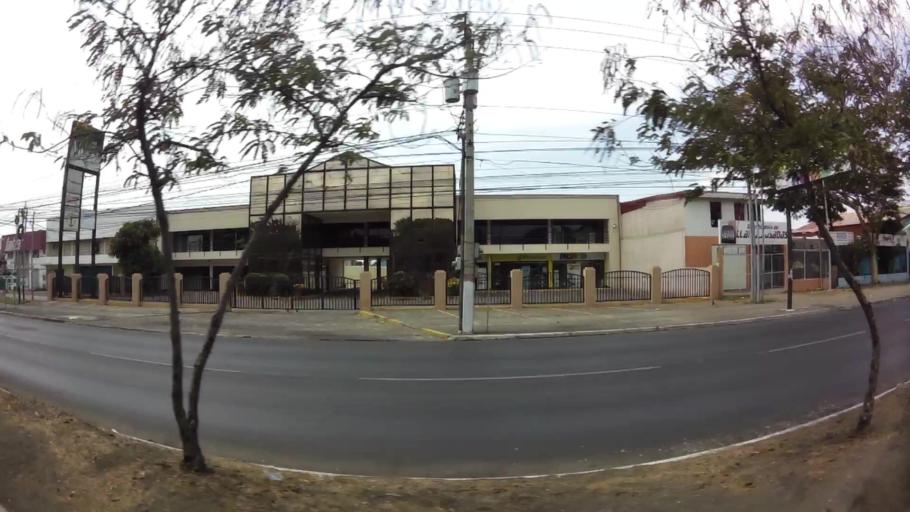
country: NI
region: Managua
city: Managua
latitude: 12.1527
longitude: -86.2472
